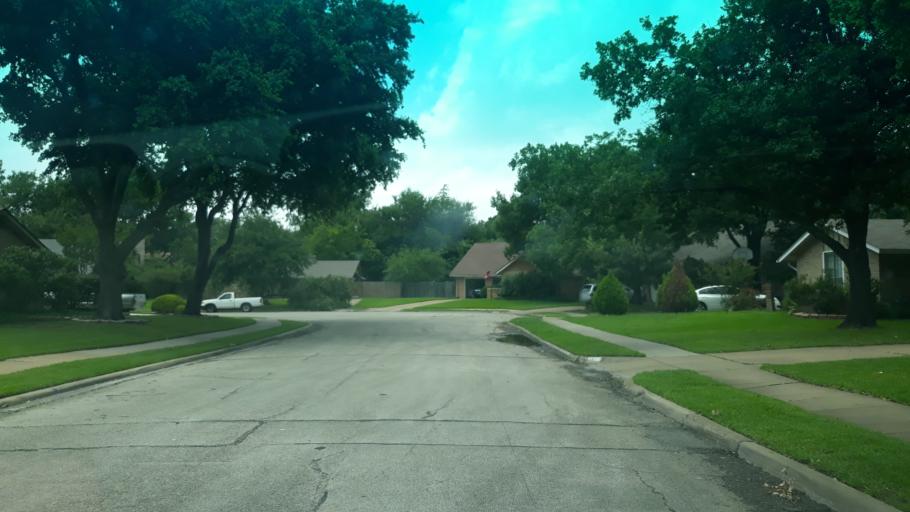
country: US
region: Texas
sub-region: Dallas County
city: Irving
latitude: 32.8574
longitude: -96.9600
